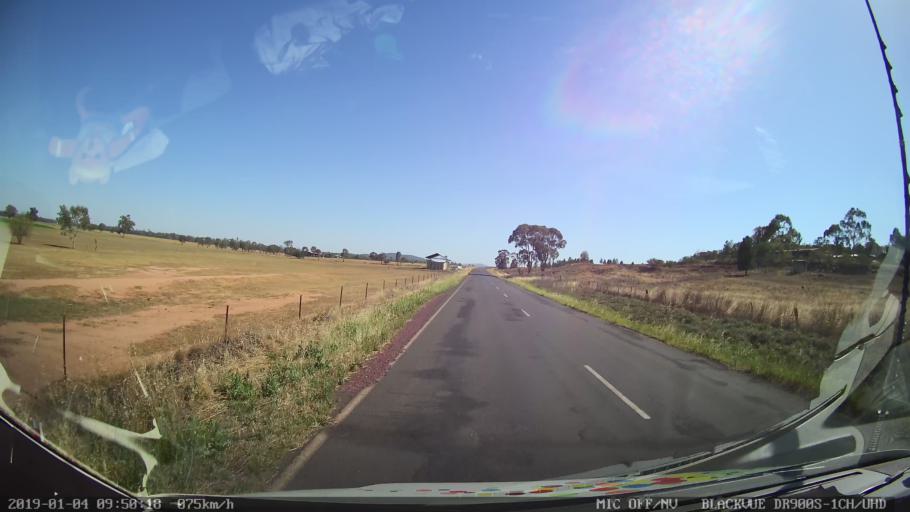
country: AU
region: New South Wales
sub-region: Cabonne
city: Canowindra
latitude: -33.5858
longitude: 148.4148
